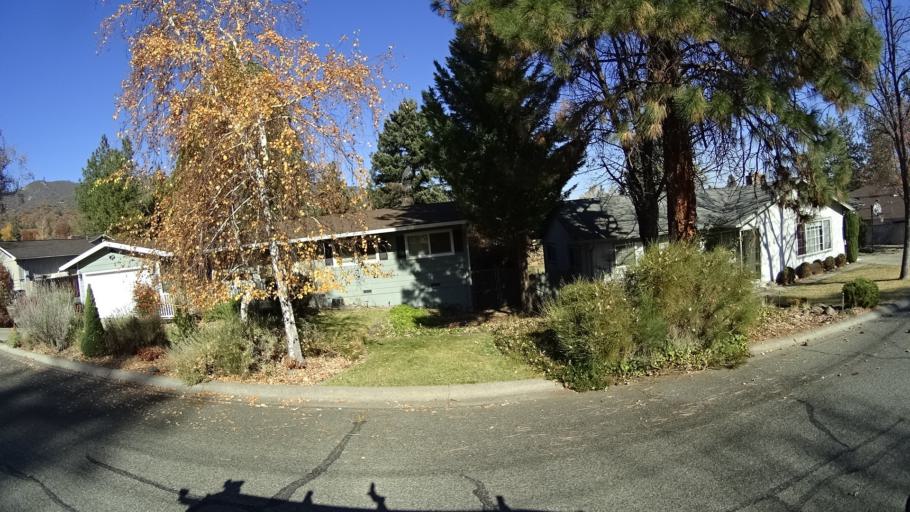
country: US
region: California
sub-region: Siskiyou County
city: Yreka
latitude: 41.7398
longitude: -122.6492
